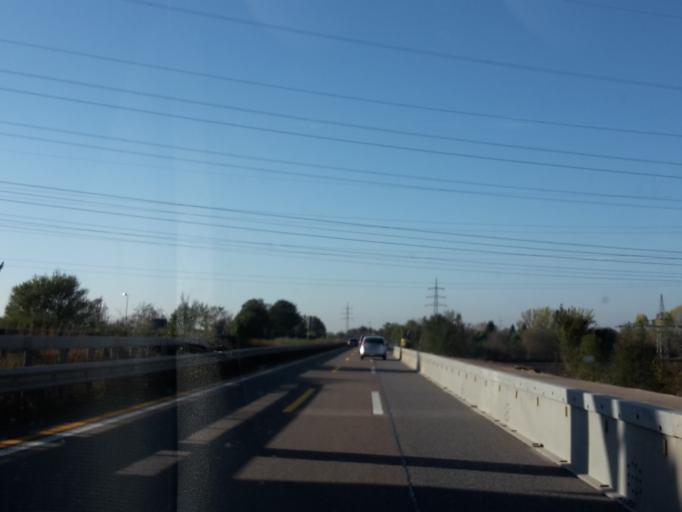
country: DE
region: Rheinland-Pfalz
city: Frankenthal
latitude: 49.5539
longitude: 8.3806
